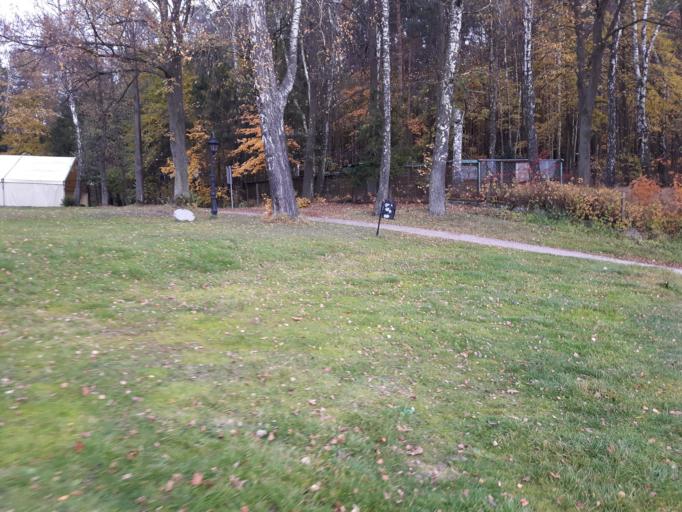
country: PL
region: Warmian-Masurian Voivodeship
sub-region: Powiat olsztynski
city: Barczewo
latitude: 53.8294
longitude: 20.7376
